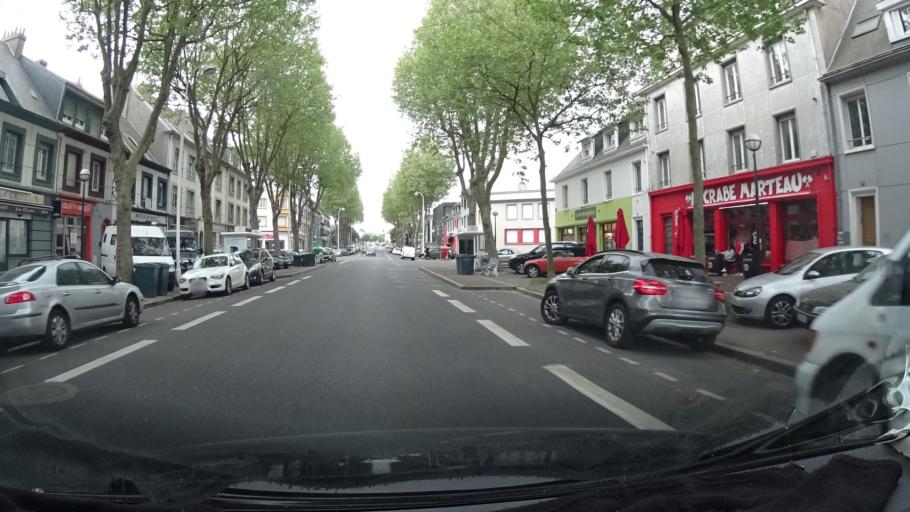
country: FR
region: Brittany
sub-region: Departement du Morbihan
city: Lorient
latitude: 47.7339
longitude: -3.3649
